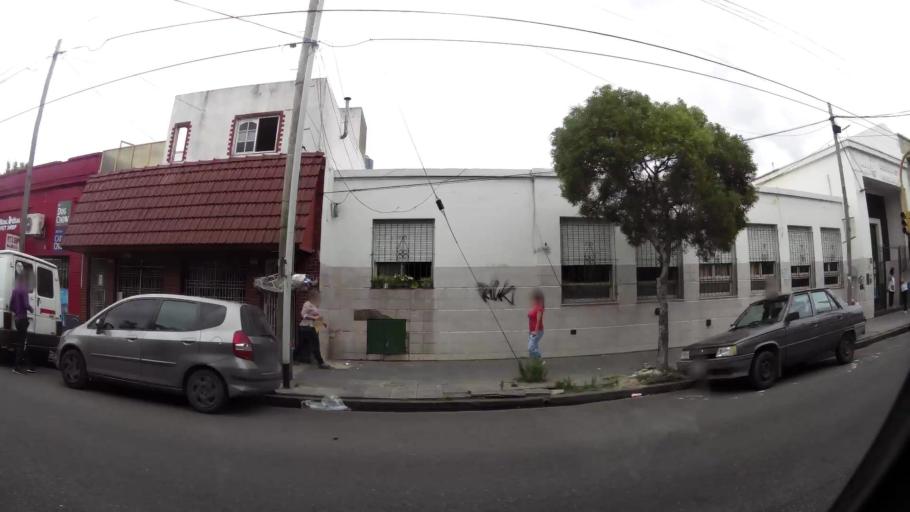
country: AR
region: Buenos Aires
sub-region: Partido de Avellaneda
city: Avellaneda
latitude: -34.6839
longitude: -58.3726
